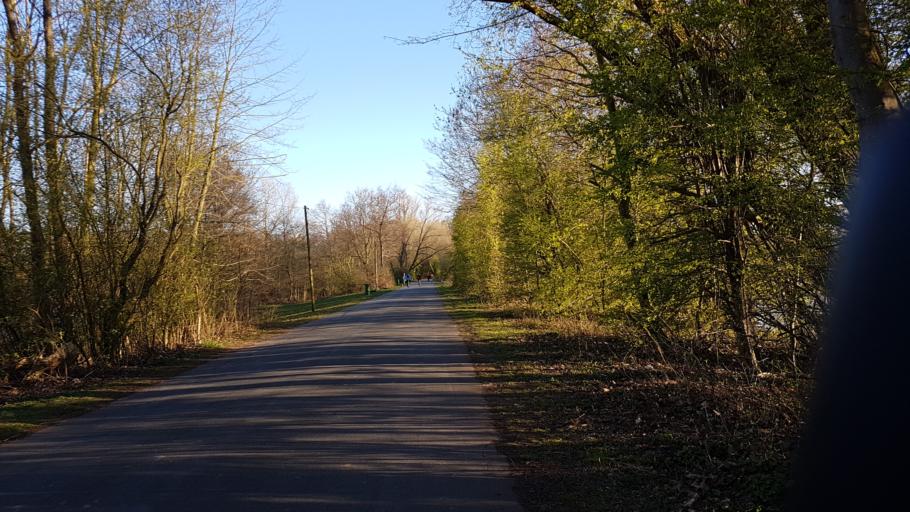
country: DE
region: Lower Saxony
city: Hannover
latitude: 52.3413
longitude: 9.7405
